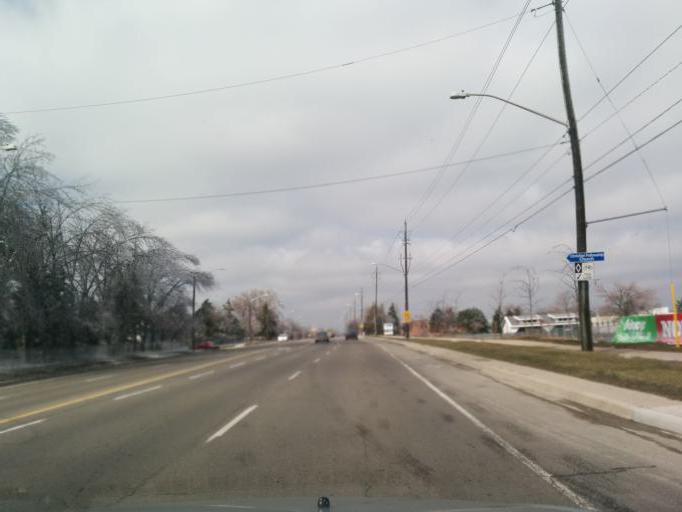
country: CA
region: Ontario
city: Waterloo
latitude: 43.4978
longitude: -80.5506
